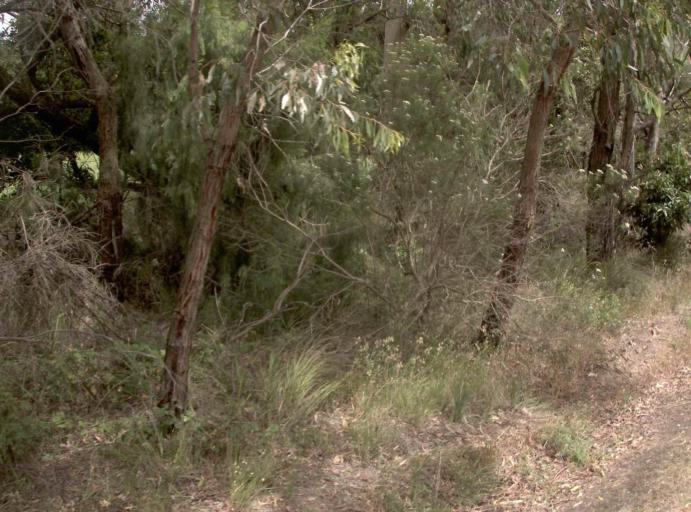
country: AU
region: Victoria
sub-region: Latrobe
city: Moe
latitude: -38.0680
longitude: 146.1750
